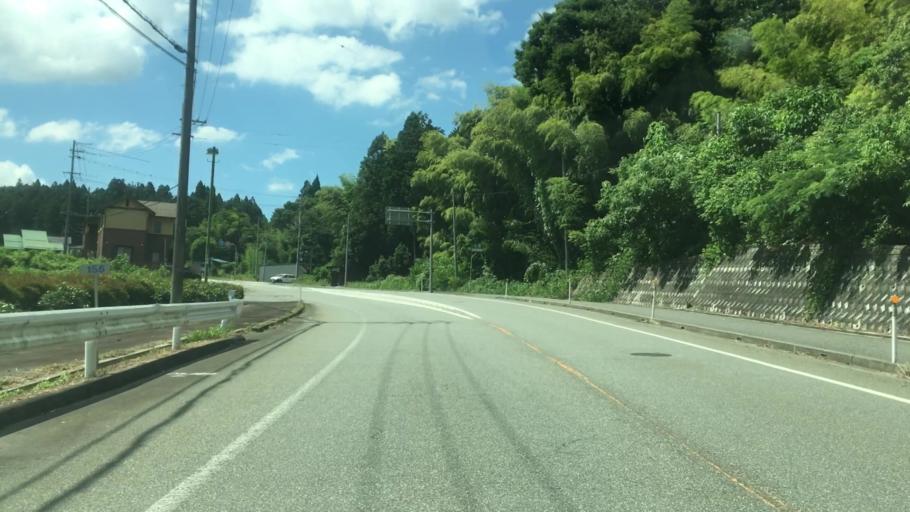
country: JP
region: Hyogo
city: Toyooka
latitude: 35.4853
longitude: 134.7043
